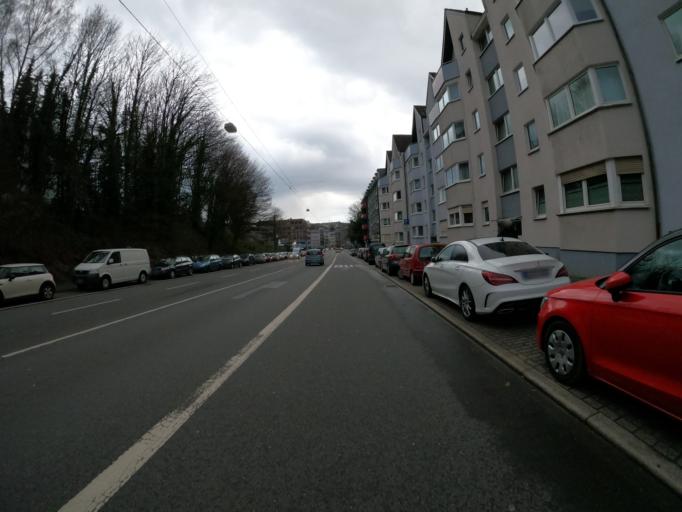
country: DE
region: North Rhine-Westphalia
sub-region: Regierungsbezirk Dusseldorf
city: Wuppertal
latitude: 51.2606
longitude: 7.1541
